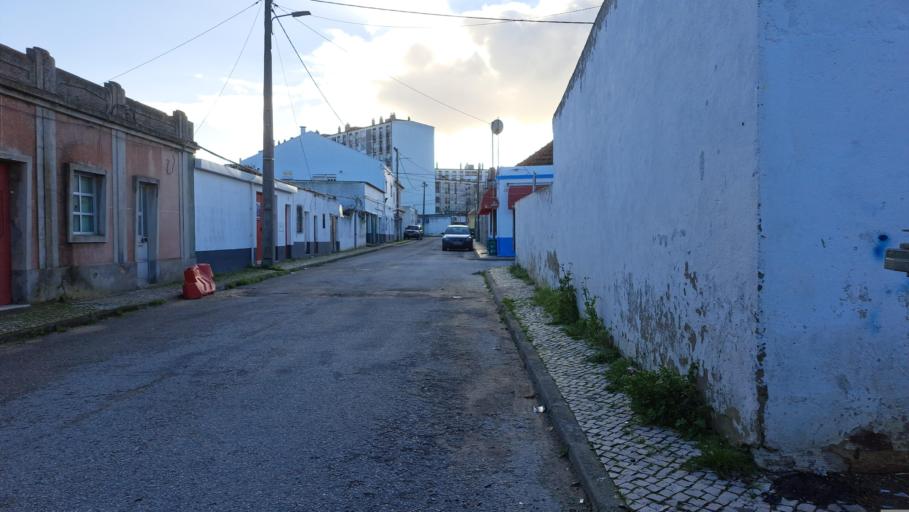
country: PT
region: Setubal
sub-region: Moita
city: Alhos Vedros
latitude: 38.6488
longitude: -9.0380
